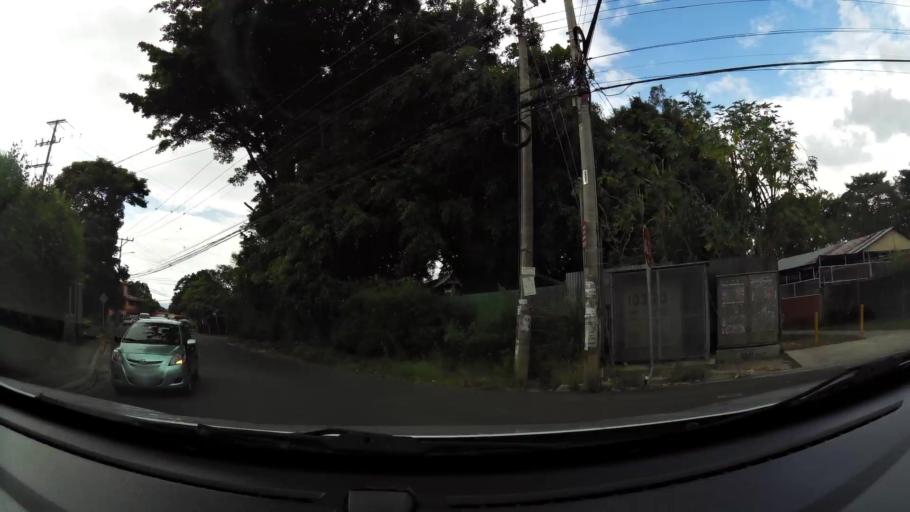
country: CR
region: San Jose
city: Escazu
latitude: 9.9251
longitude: -84.1451
